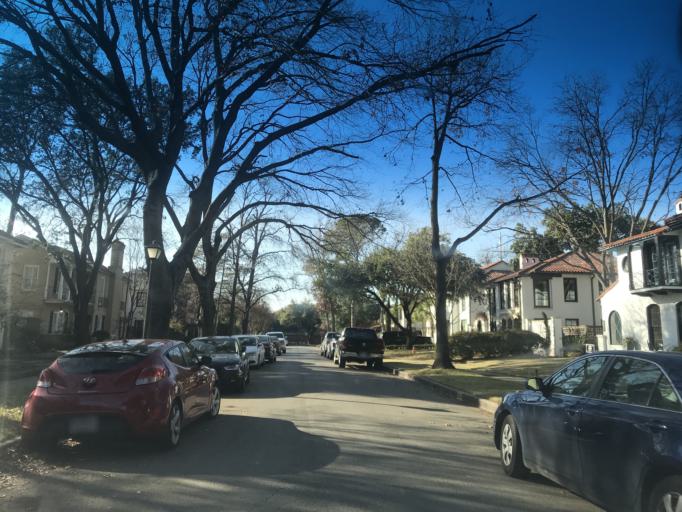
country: US
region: Texas
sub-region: Dallas County
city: Highland Park
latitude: 32.8231
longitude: -96.8150
